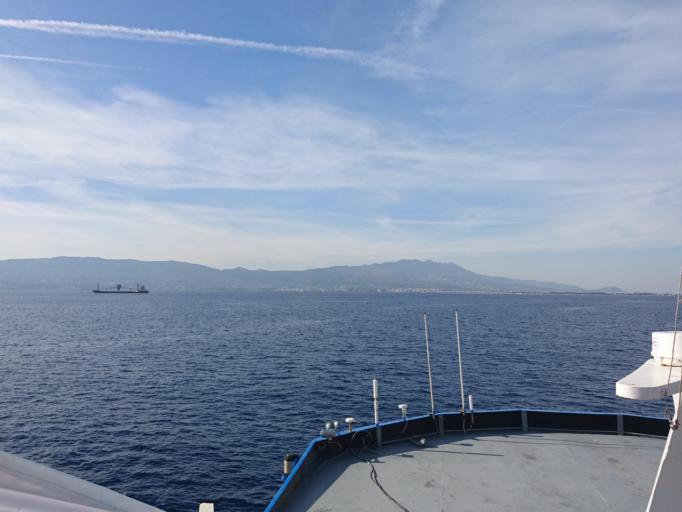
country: GR
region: South Aegean
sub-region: Nomos Dodekanisou
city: Kos
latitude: 36.9362
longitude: 27.3311
